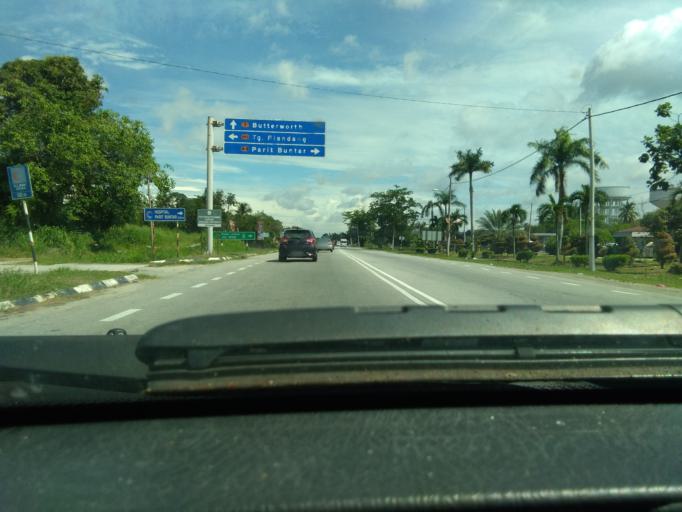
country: MY
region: Perak
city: Parit Buntar
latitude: 5.1089
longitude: 100.4832
